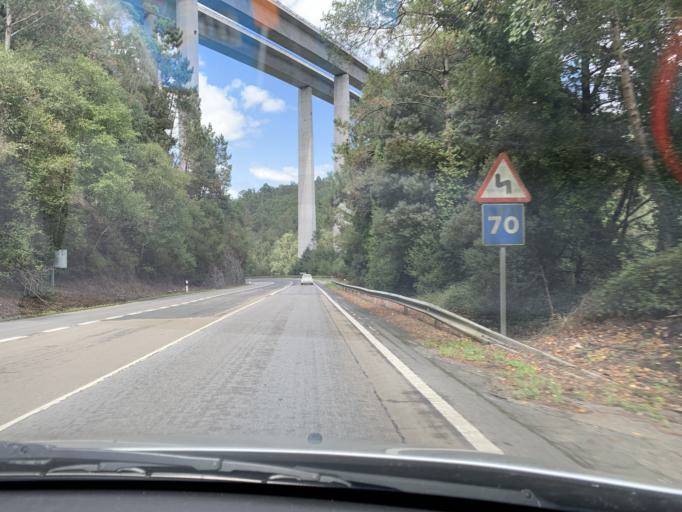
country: ES
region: Galicia
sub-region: Provincia de Lugo
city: Barreiros
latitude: 43.5042
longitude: -7.2711
